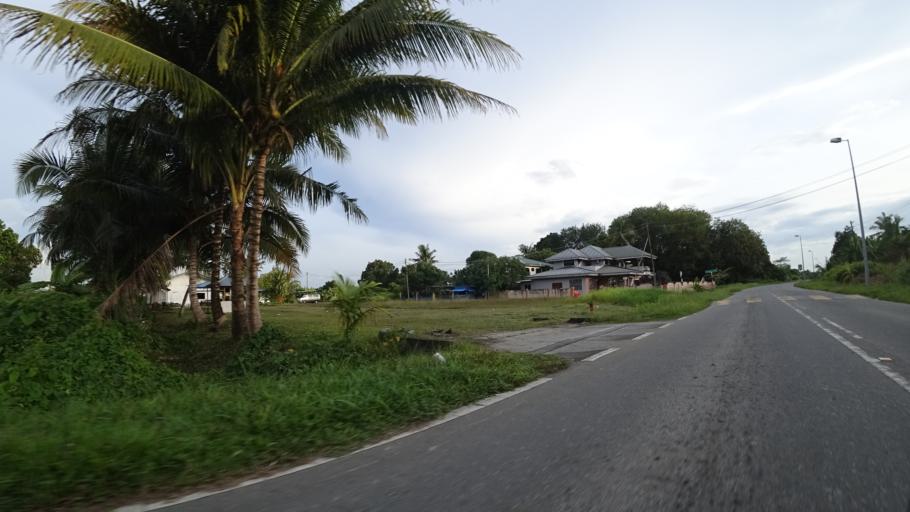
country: BN
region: Tutong
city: Tutong
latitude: 4.8278
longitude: 114.8188
